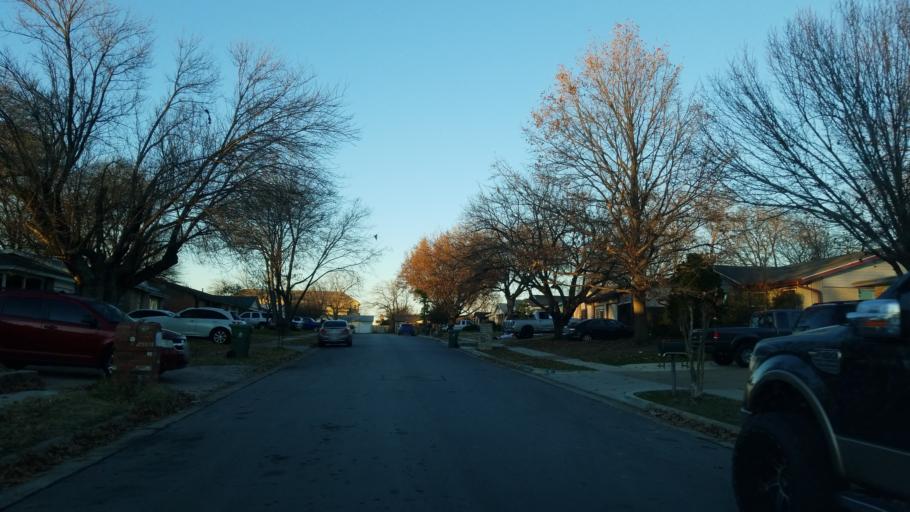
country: US
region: Texas
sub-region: Tarrant County
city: Arlington
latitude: 32.7310
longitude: -97.0572
